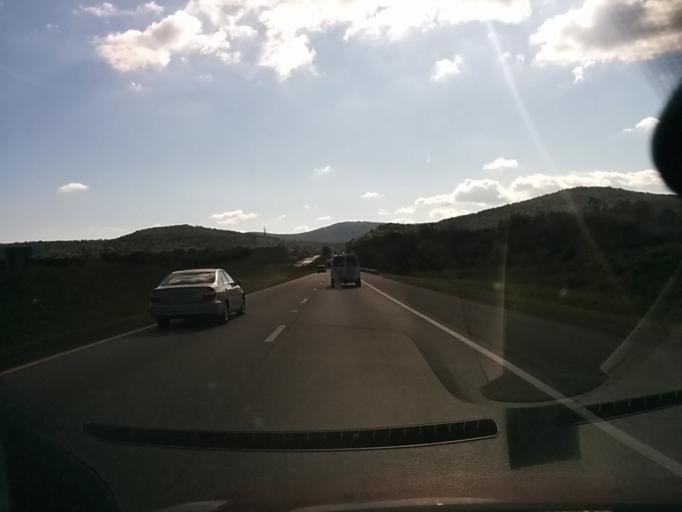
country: US
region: Virginia
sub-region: City of Waynesboro
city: Waynesboro
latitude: 38.0529
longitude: -78.9174
